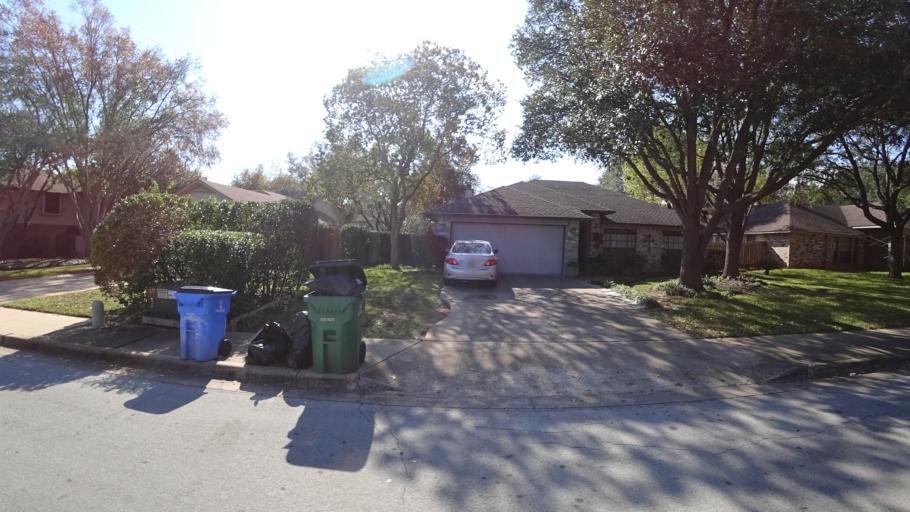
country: US
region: Texas
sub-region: Travis County
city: Shady Hollow
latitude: 30.1726
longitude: -97.8681
